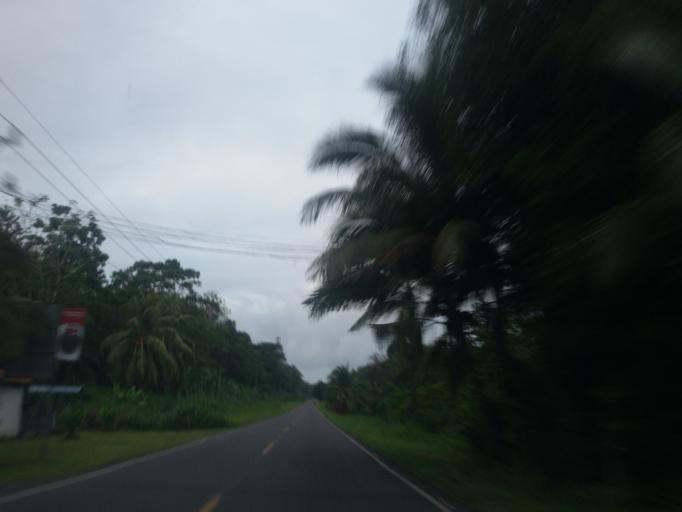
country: PA
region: Bocas del Toro
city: Barranco
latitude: 9.6992
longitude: -82.8158
